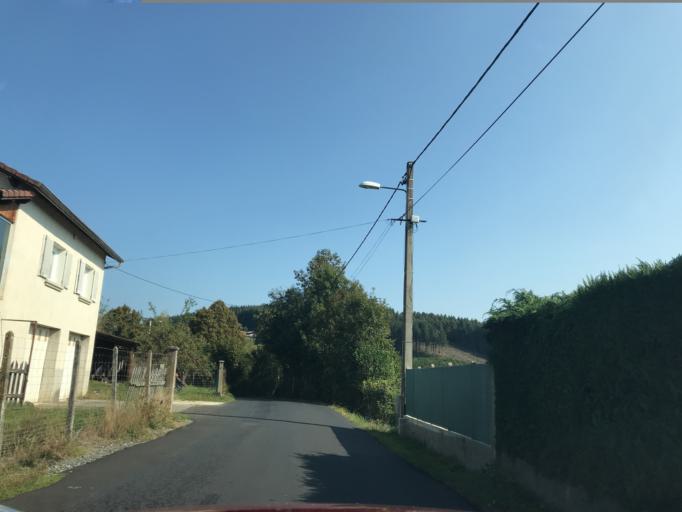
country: FR
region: Auvergne
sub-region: Departement du Puy-de-Dome
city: Saint-Remy-sur-Durolle
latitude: 45.8806
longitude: 3.6019
